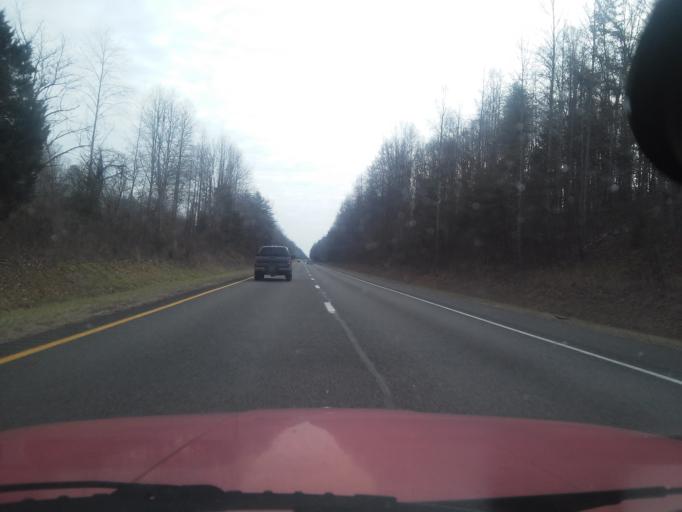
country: US
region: Virginia
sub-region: Louisa County
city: Louisa
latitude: 37.8684
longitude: -78.0113
